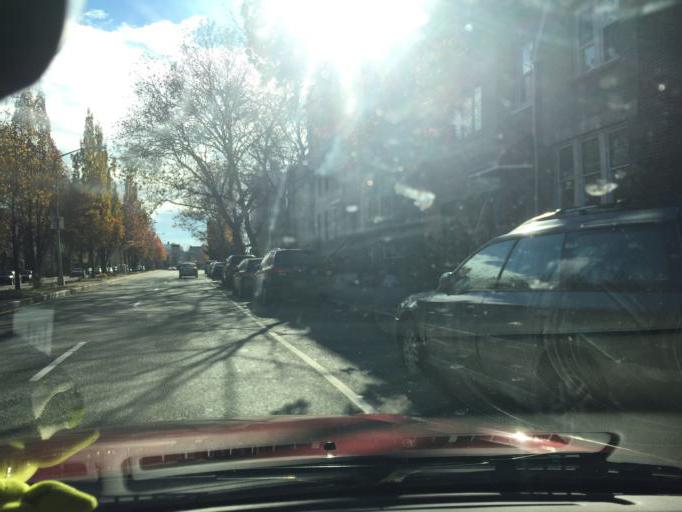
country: US
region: New York
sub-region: Queens County
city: Long Island City
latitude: 40.7244
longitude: -73.9481
